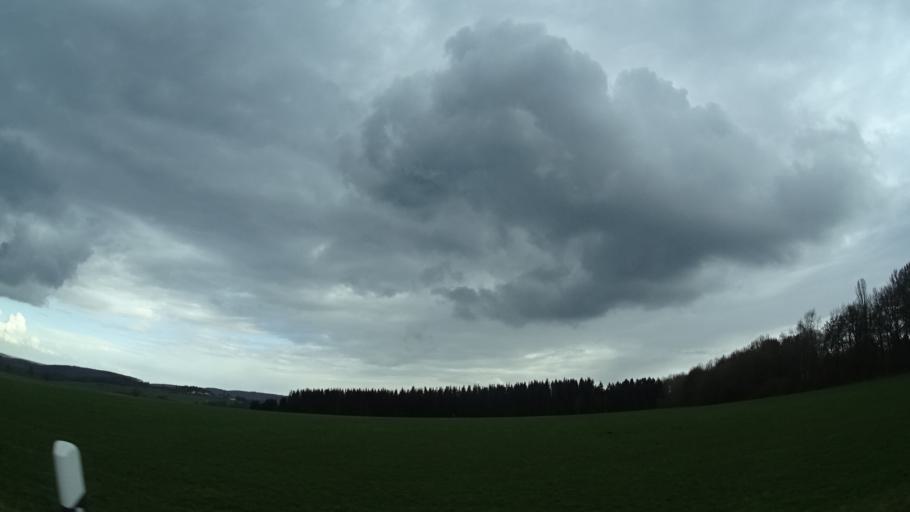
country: DE
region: Rheinland-Pfalz
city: Dorrebach
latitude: 49.9566
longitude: 7.6995
